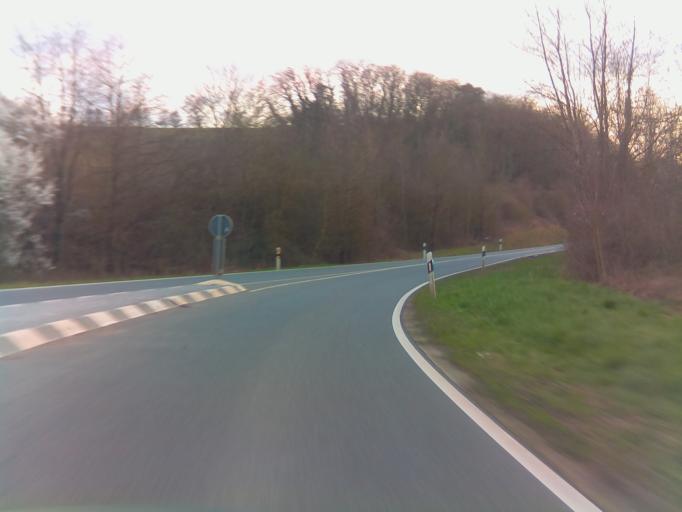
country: DE
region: Rheinland-Pfalz
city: Wendelsheim
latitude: 49.7739
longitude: 8.0186
